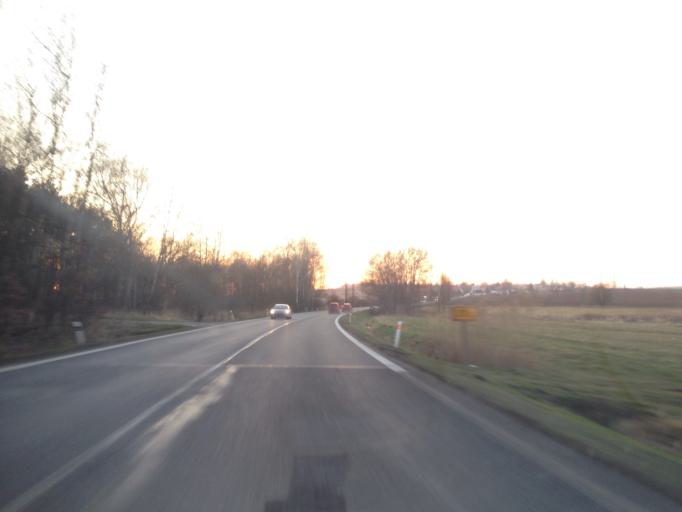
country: CZ
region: Central Bohemia
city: Revnicov
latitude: 50.1754
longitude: 13.8233
